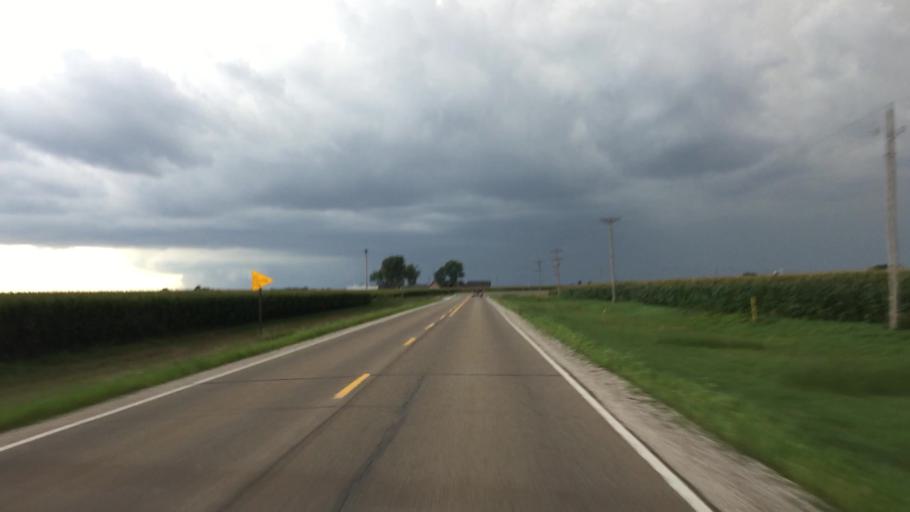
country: US
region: Iowa
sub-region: Henry County
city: New London
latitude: 40.7732
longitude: -91.4710
